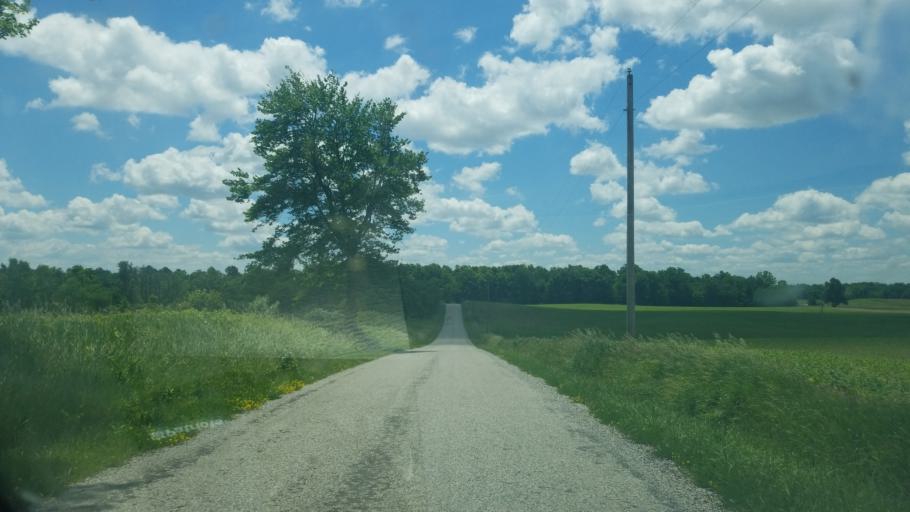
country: US
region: Ohio
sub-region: Ashland County
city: Ashland
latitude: 40.9842
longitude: -82.3266
